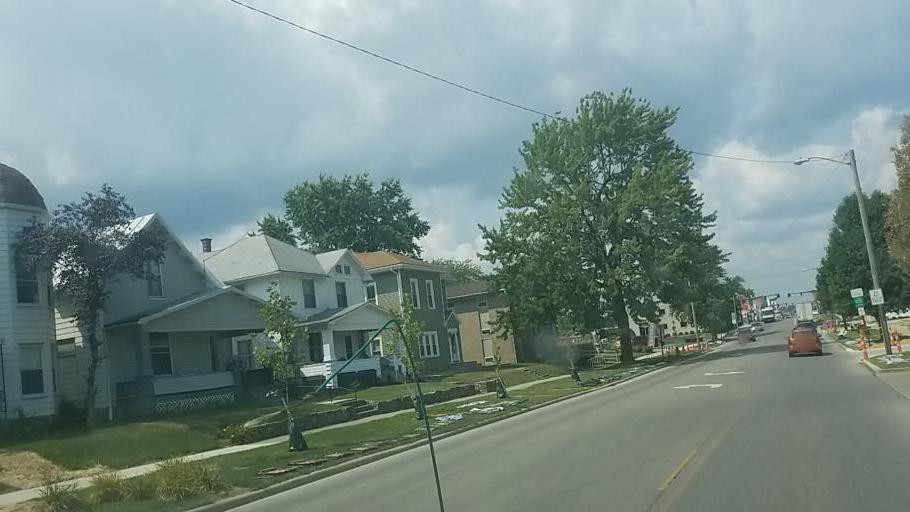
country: US
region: Ohio
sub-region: Crawford County
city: Bucyrus
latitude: 40.8036
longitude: -82.9755
